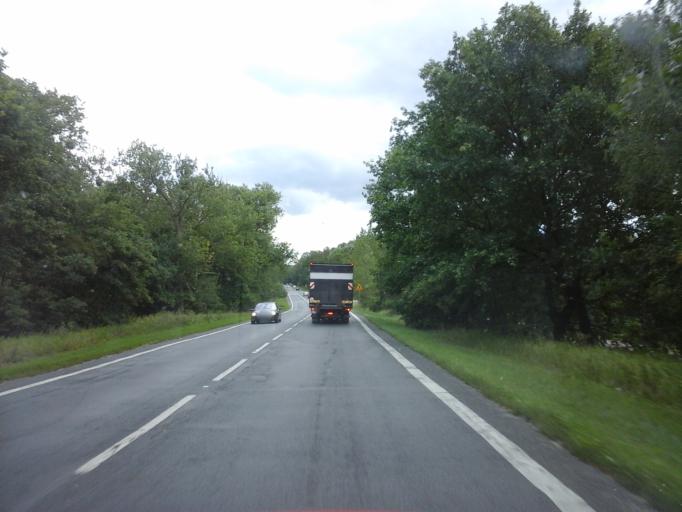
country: PL
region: West Pomeranian Voivodeship
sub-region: Szczecin
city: Szczecin
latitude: 53.3803
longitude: 14.5418
